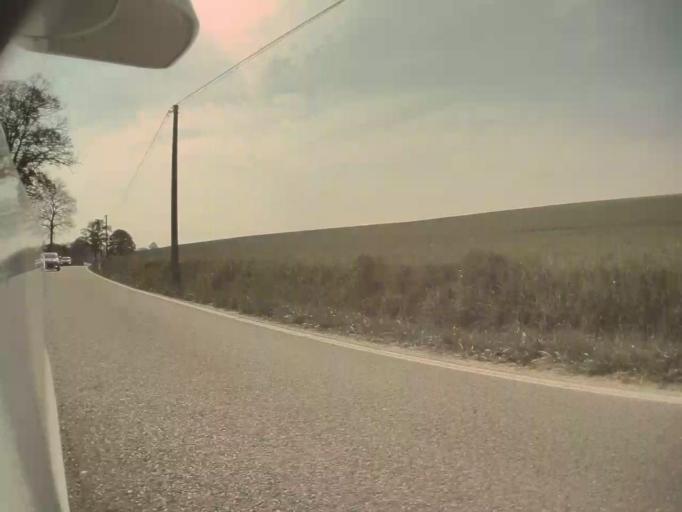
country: BE
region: Wallonia
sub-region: Province de Namur
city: Havelange
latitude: 50.3334
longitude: 5.2790
